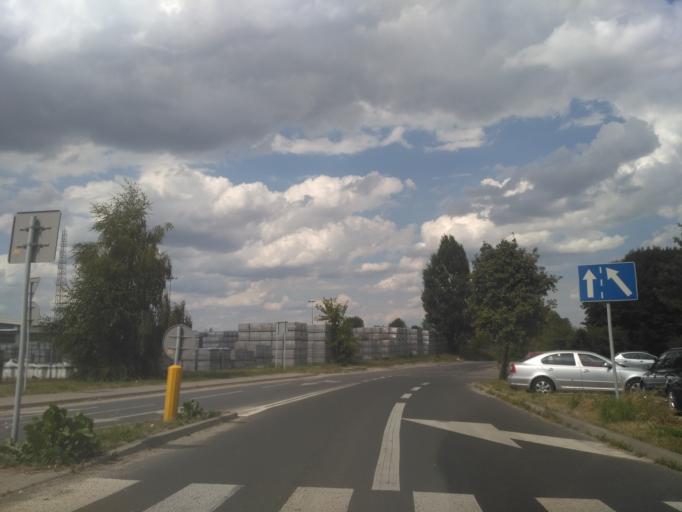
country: PL
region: Lublin Voivodeship
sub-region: Powiat lubelski
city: Jakubowice Murowane
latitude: 51.2331
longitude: 22.6167
